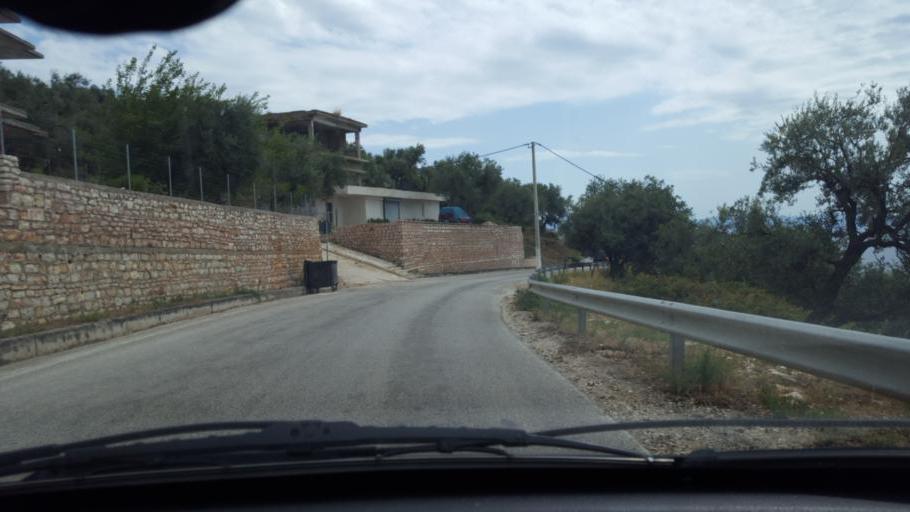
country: AL
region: Vlore
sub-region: Rrethi i Sarandes
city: Lukove
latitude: 39.9895
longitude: 19.9153
